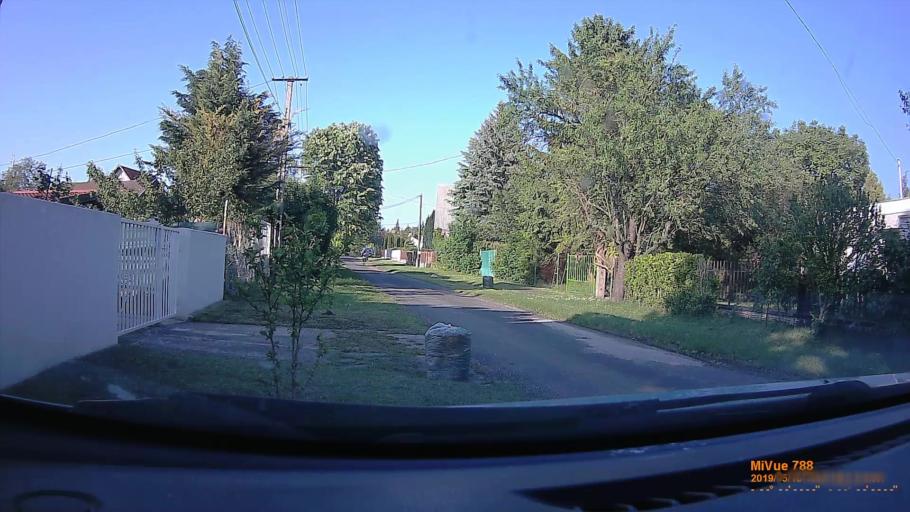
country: HU
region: Somogy
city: Balatonszabadi
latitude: 46.9434
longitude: 18.1417
